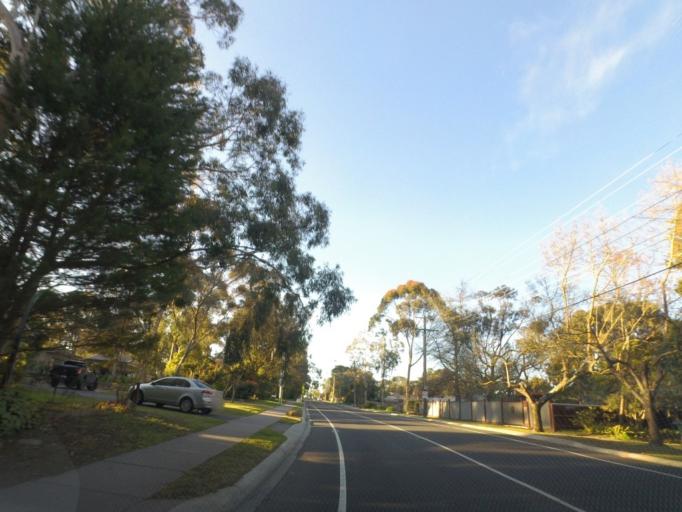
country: AU
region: Victoria
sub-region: Manningham
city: Park Orchards
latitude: -37.7811
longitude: 145.2105
